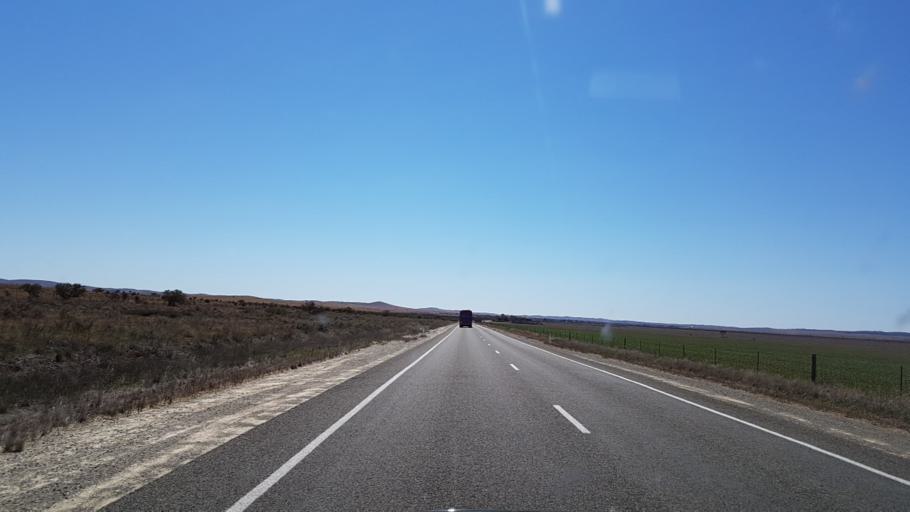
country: AU
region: South Australia
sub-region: Peterborough
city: Peterborough
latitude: -33.1983
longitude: 138.9005
